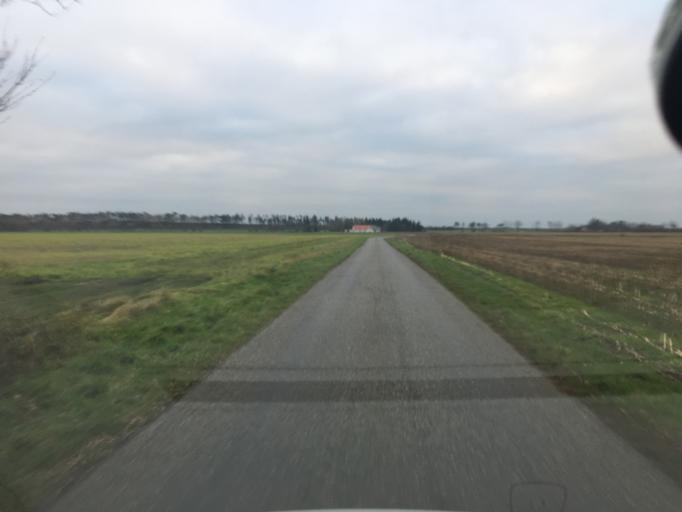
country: DK
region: South Denmark
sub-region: Tonder Kommune
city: Logumkloster
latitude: 55.0577
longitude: 9.0651
